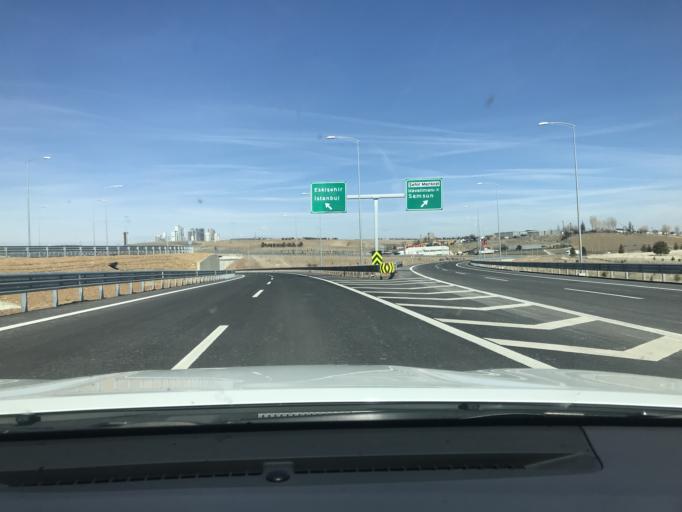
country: TR
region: Ankara
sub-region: Goelbasi
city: Golbasi
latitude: 39.7852
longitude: 32.7464
